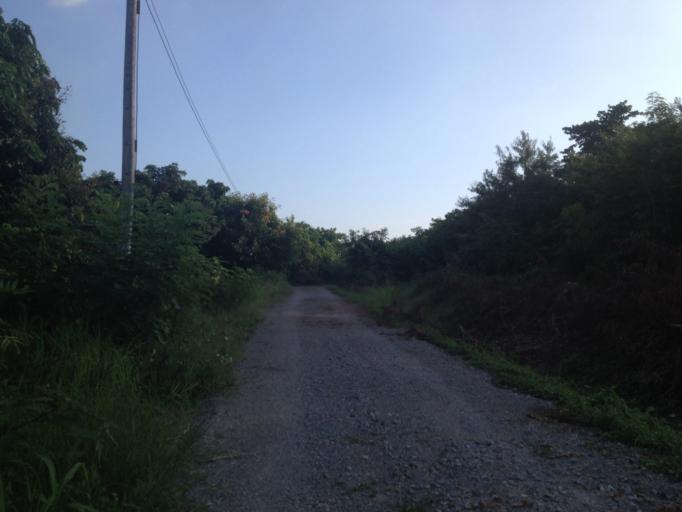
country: TH
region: Chiang Mai
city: Hang Dong
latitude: 18.6831
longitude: 98.9006
